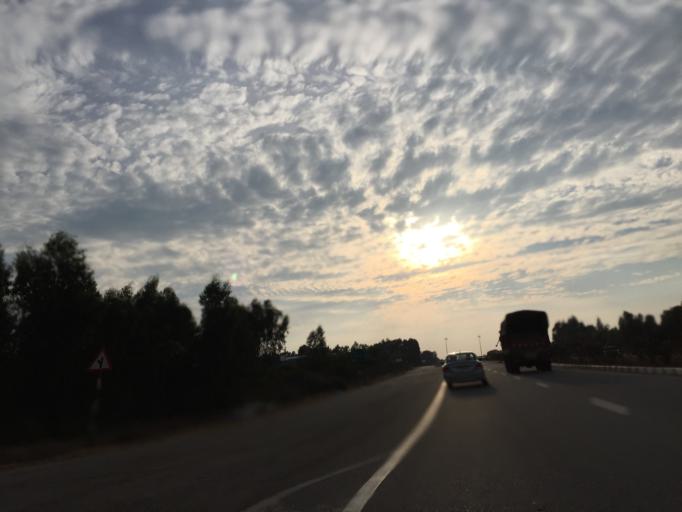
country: IN
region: Karnataka
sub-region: Kolar
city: Kolar
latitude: 13.1434
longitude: 78.2366
